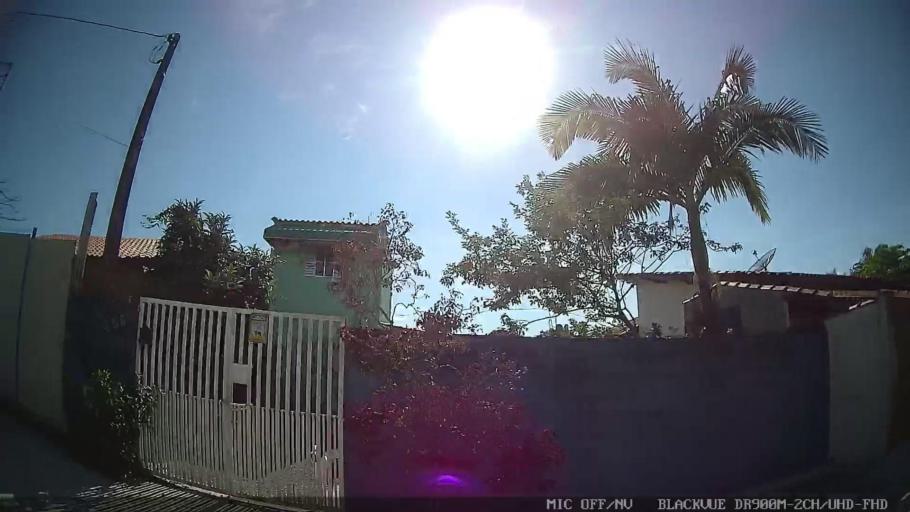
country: BR
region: Sao Paulo
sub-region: Itanhaem
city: Itanhaem
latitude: -24.2179
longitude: -46.8661
